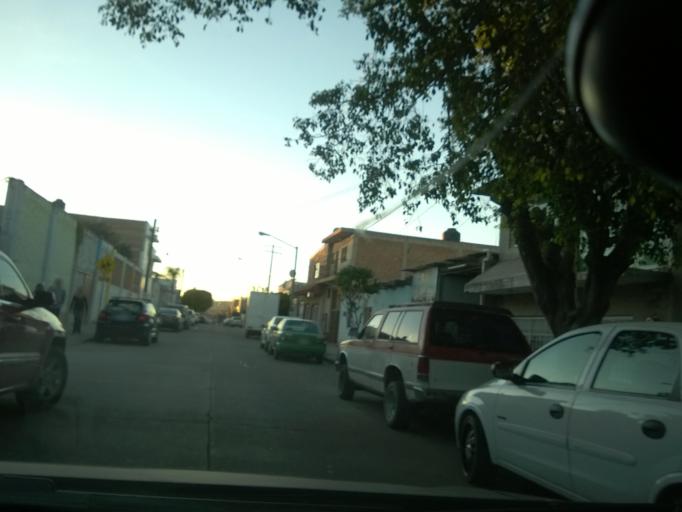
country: MX
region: Guanajuato
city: Leon
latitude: 21.1020
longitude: -101.6796
